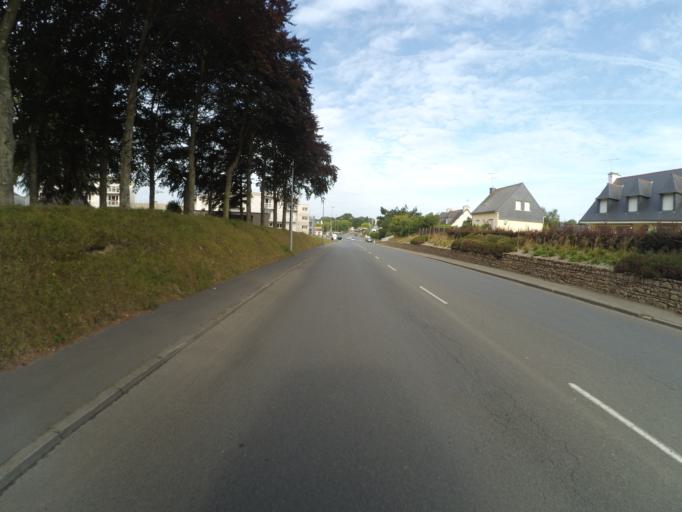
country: FR
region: Brittany
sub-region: Departement des Cotes-d'Armor
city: Guingamp
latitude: 48.5630
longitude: -3.1626
